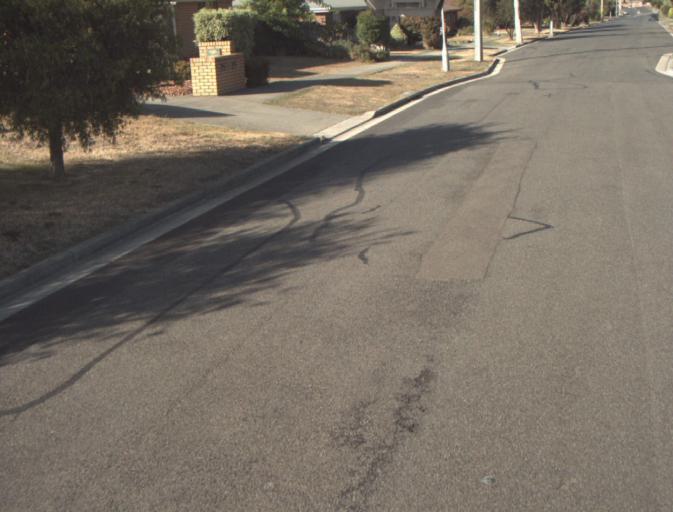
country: AU
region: Tasmania
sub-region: Launceston
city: Newnham
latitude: -41.3949
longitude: 147.1324
